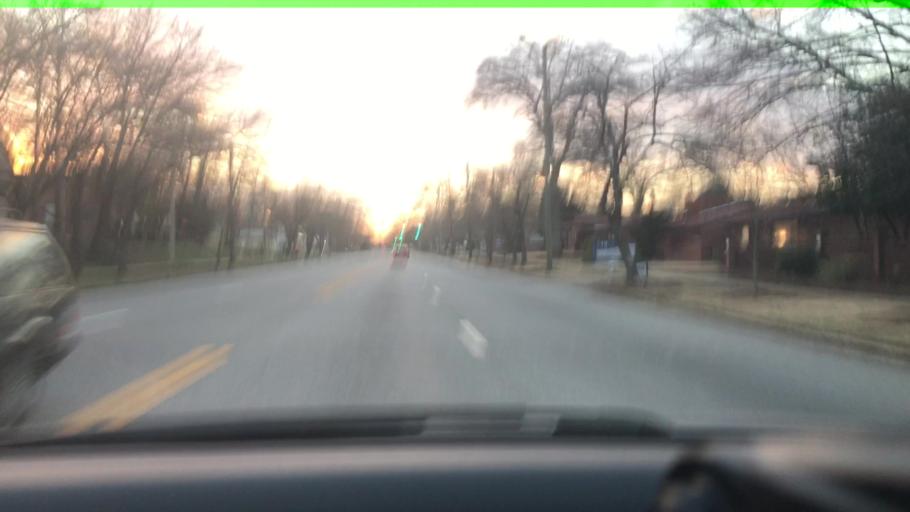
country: US
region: Georgia
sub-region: Clarke County
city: Athens
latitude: 33.9613
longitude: -83.3889
